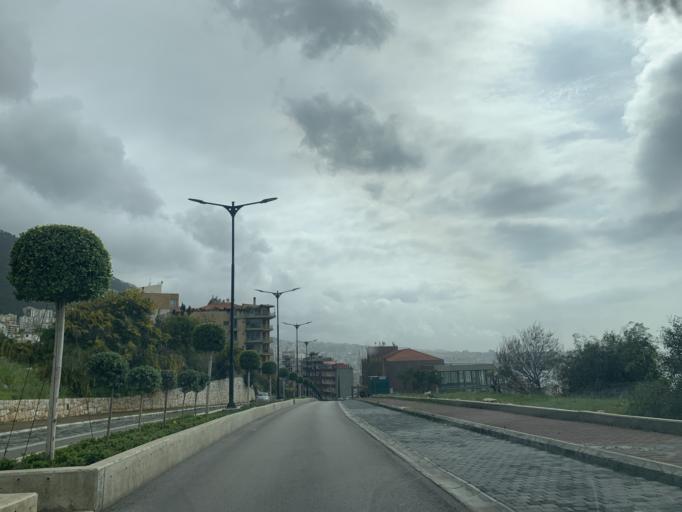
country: LB
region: Mont-Liban
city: Djounie
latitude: 33.9987
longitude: 35.6473
